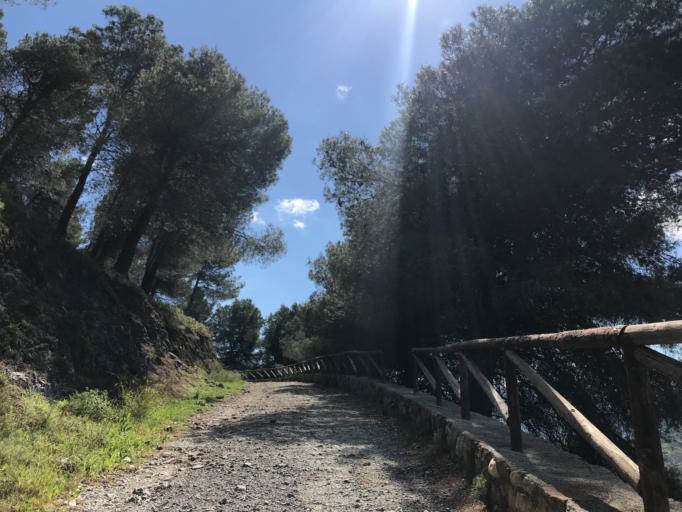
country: ES
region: Andalusia
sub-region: Provincia de Malaga
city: Alcaucin
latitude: 36.9078
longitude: -4.1082
